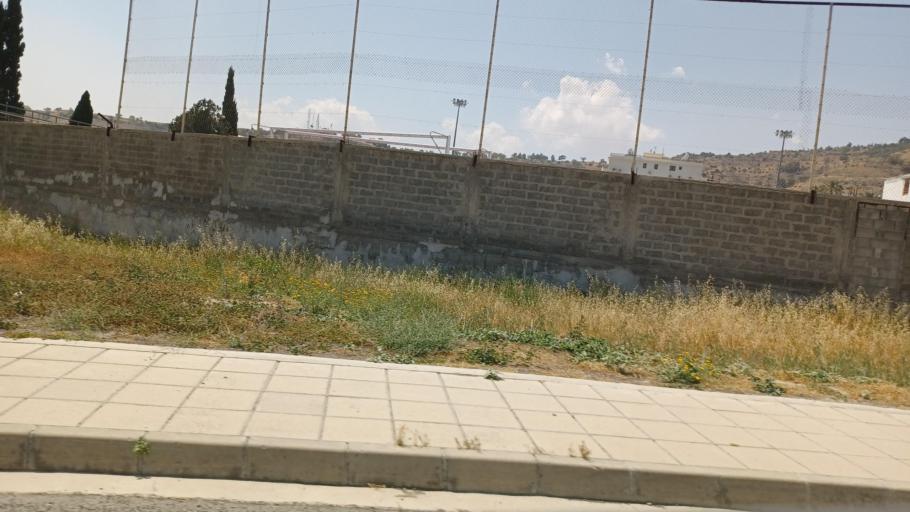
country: CY
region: Larnaka
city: Voroklini
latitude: 34.9871
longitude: 33.6573
